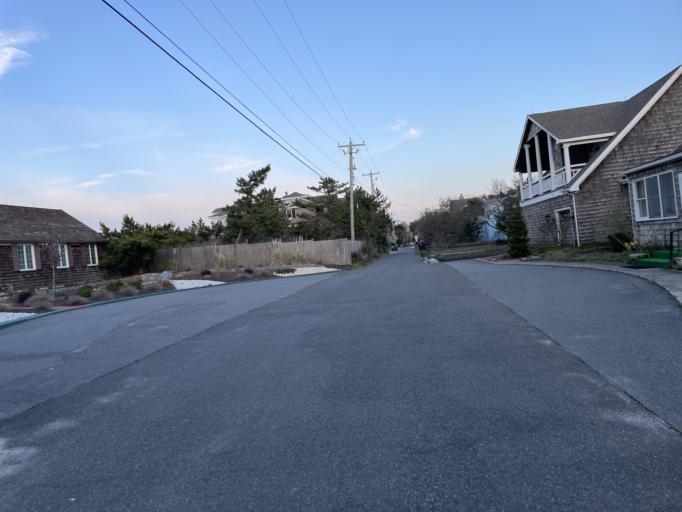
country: US
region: Delaware
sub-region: Sussex County
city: Lewes
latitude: 38.7853
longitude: -75.1488
